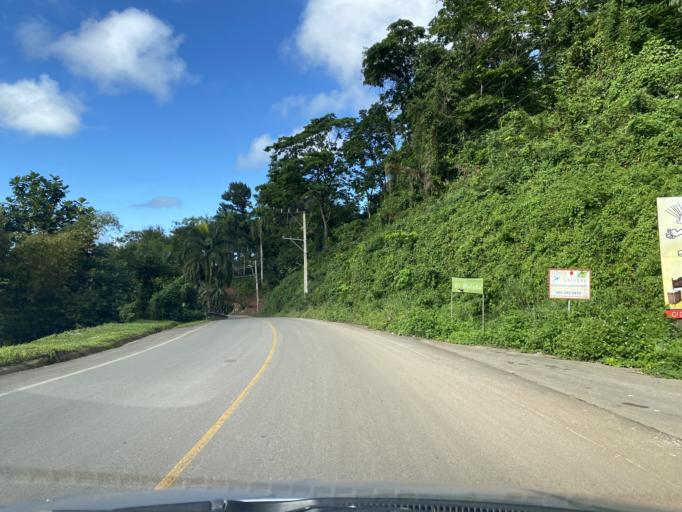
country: DO
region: Samana
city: Las Terrenas
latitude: 19.2847
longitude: -69.5518
